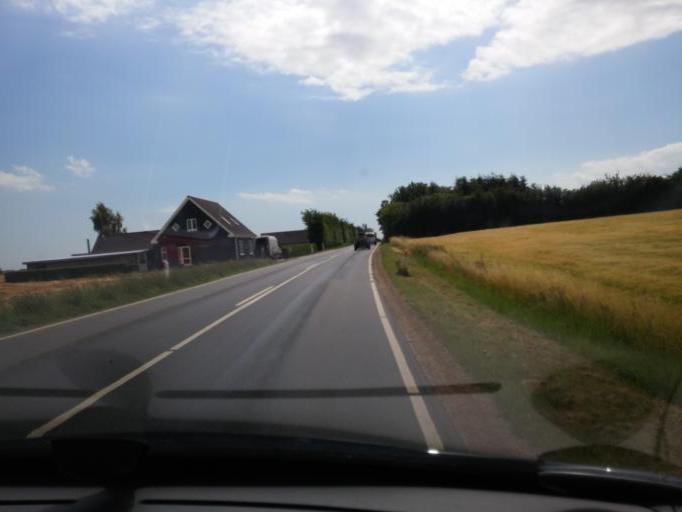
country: DK
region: South Denmark
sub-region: Langeland Kommune
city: Rudkobing
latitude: 54.8961
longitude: 10.7383
